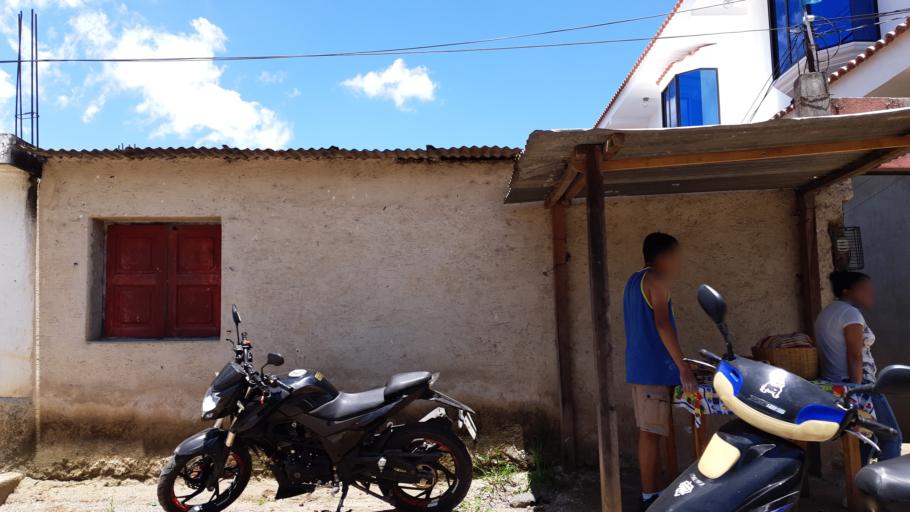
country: GT
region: Chimaltenango
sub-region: Municipio de Chimaltenango
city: Chimaltenango
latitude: 14.6621
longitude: -90.8388
